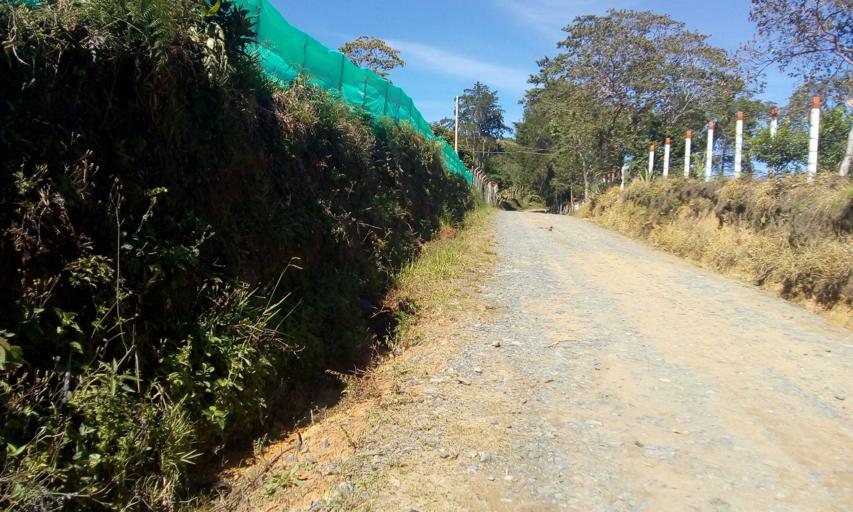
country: CO
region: Santander
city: Guepsa
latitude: 6.0012
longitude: -73.5564
